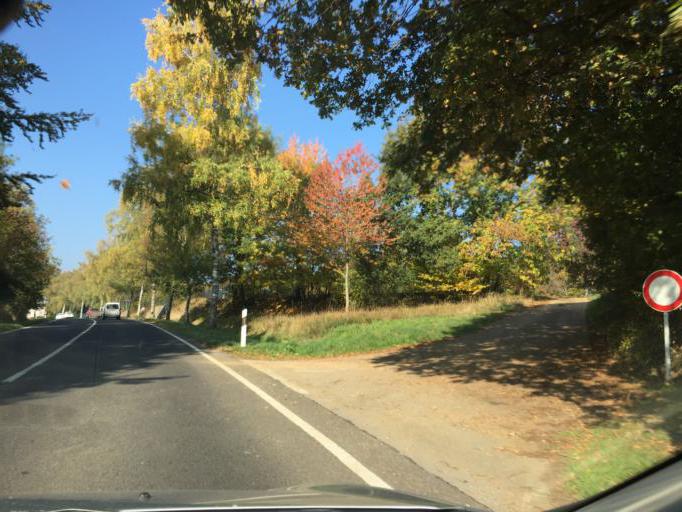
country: LU
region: Grevenmacher
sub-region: Canton de Remich
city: Waldbredimus
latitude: 49.5435
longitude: 6.2827
